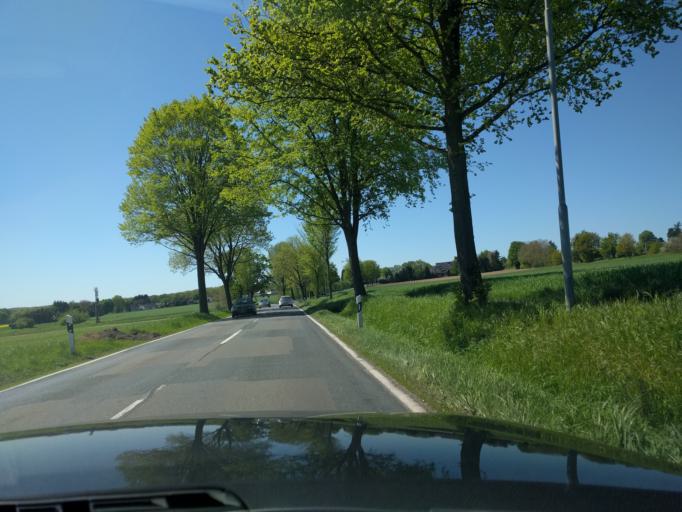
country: DE
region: Lower Saxony
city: Seevetal
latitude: 53.4070
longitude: 10.0109
